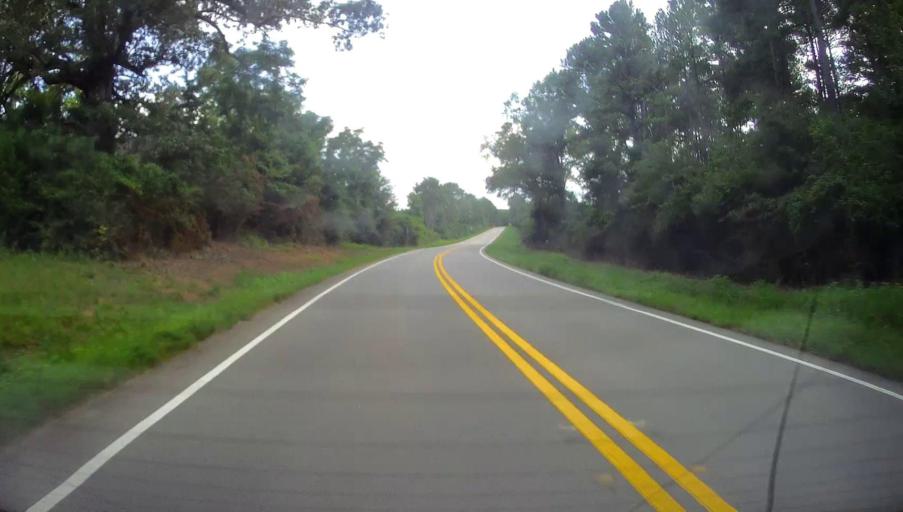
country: US
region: Georgia
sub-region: Monroe County
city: Forsyth
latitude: 33.0037
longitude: -83.9397
